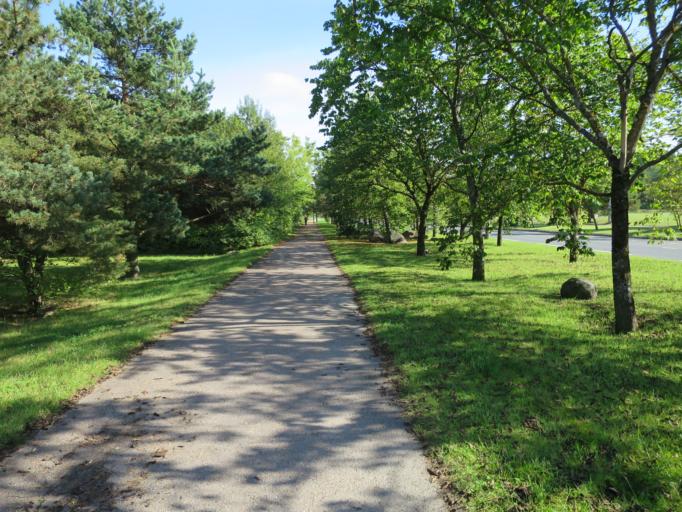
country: EE
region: Harju
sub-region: Tallinna linn
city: Tallinn
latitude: 59.3964
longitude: 24.7011
